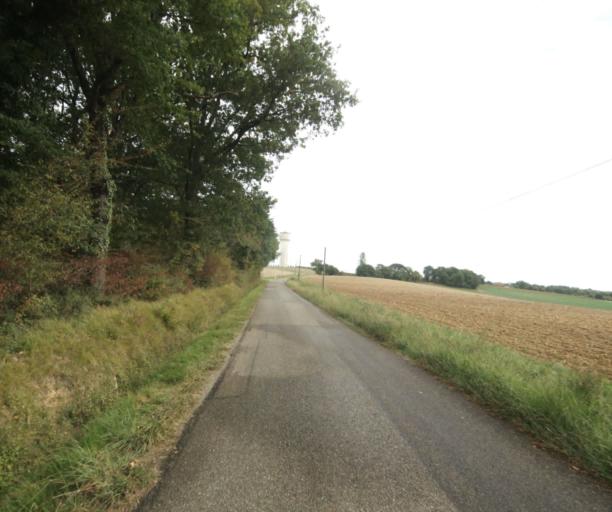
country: FR
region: Midi-Pyrenees
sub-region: Departement du Gers
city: Cazaubon
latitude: 43.8924
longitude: -0.1191
